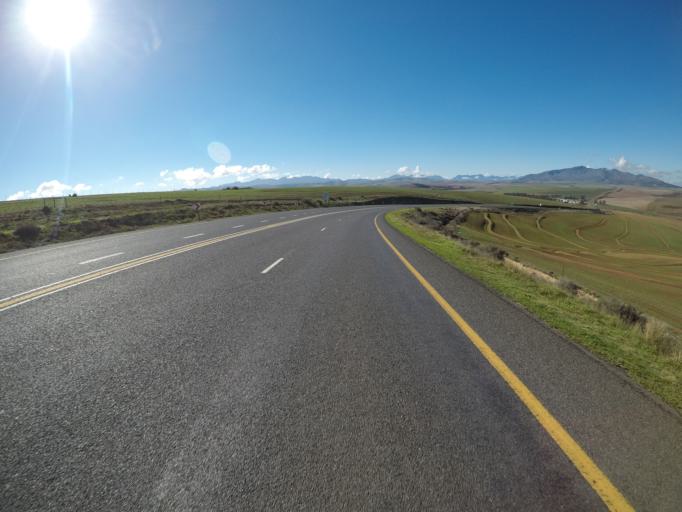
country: ZA
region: Western Cape
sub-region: Overberg District Municipality
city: Caledon
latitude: -34.2128
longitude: 19.3216
